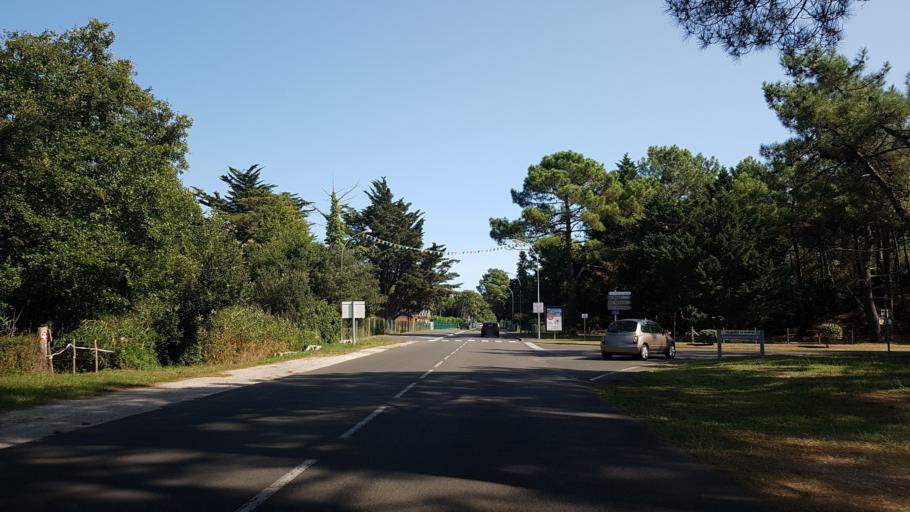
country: FR
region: Poitou-Charentes
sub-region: Departement de la Charente-Maritime
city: Les Mathes
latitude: 45.6936
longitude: -1.1883
